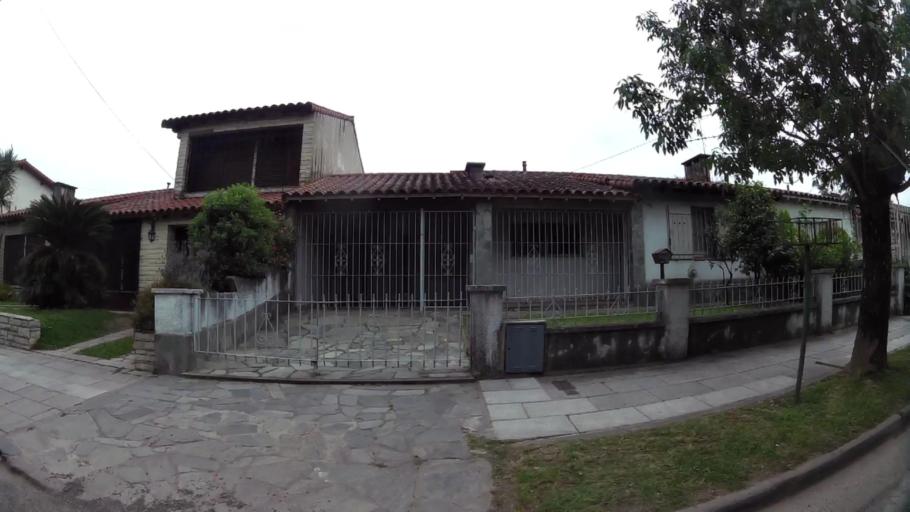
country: AR
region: Buenos Aires
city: San Justo
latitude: -34.7149
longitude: -58.5355
